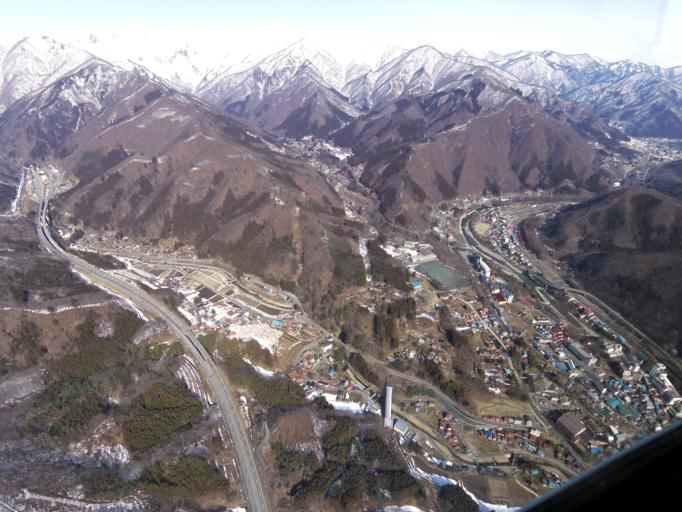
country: JP
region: Gunma
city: Numata
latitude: 36.7667
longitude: 138.9641
